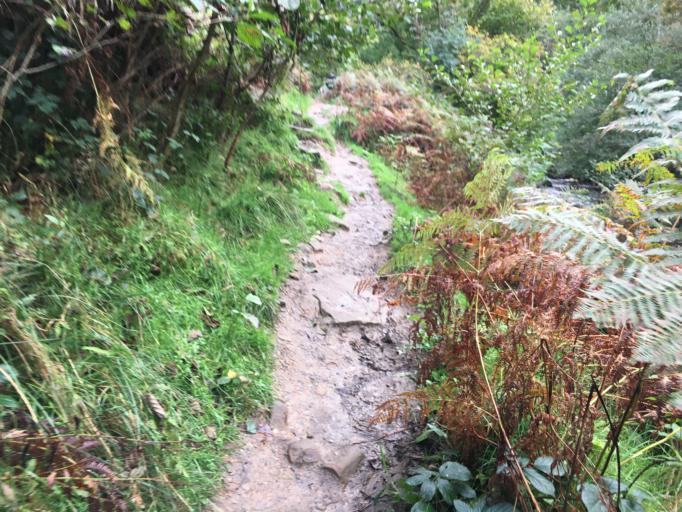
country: GB
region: England
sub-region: North Yorkshire
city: Sleights
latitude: 54.4086
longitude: -0.7317
